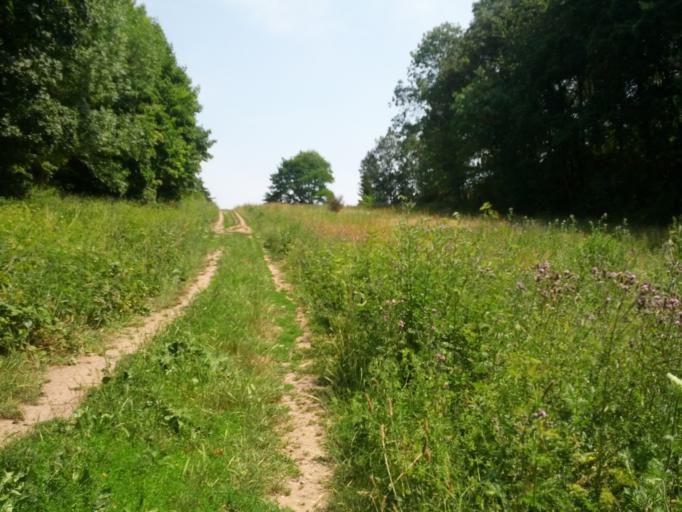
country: DE
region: Thuringia
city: Eisenach
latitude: 50.9868
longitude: 10.2899
